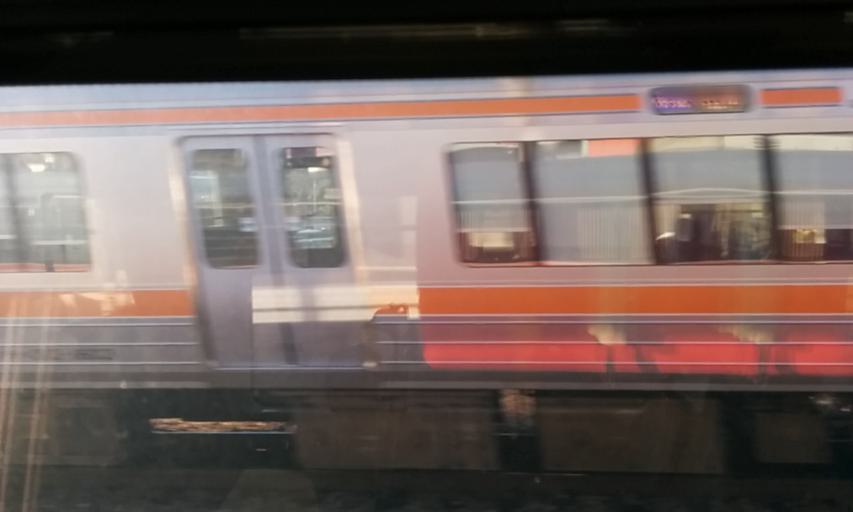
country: JP
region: Gifu
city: Nakatsugawa
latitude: 35.5030
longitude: 137.5040
